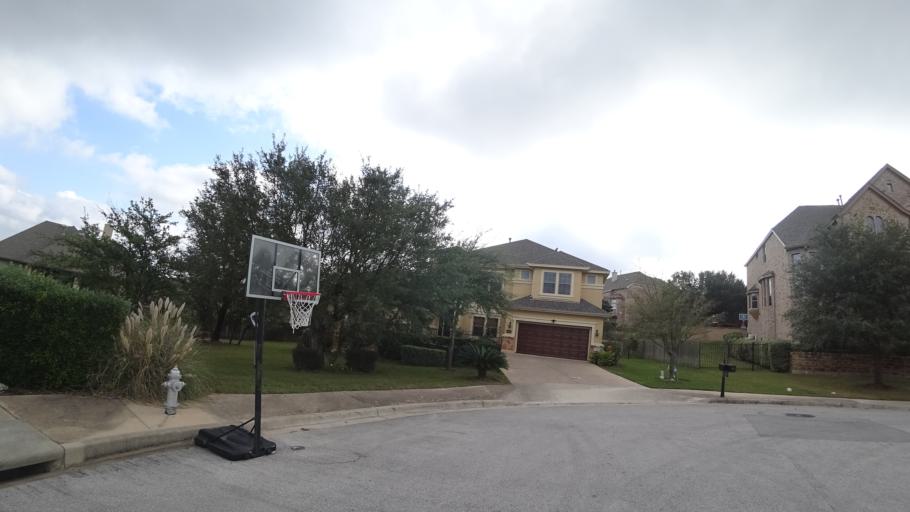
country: US
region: Texas
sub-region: Travis County
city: Barton Creek
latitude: 30.3158
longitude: -97.8990
